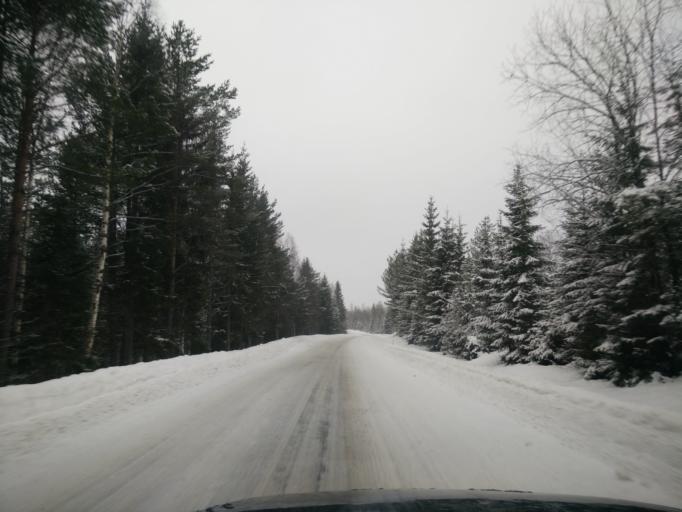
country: SE
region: Vaesternorrland
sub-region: Ange Kommun
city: Ange
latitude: 62.4649
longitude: 15.4450
